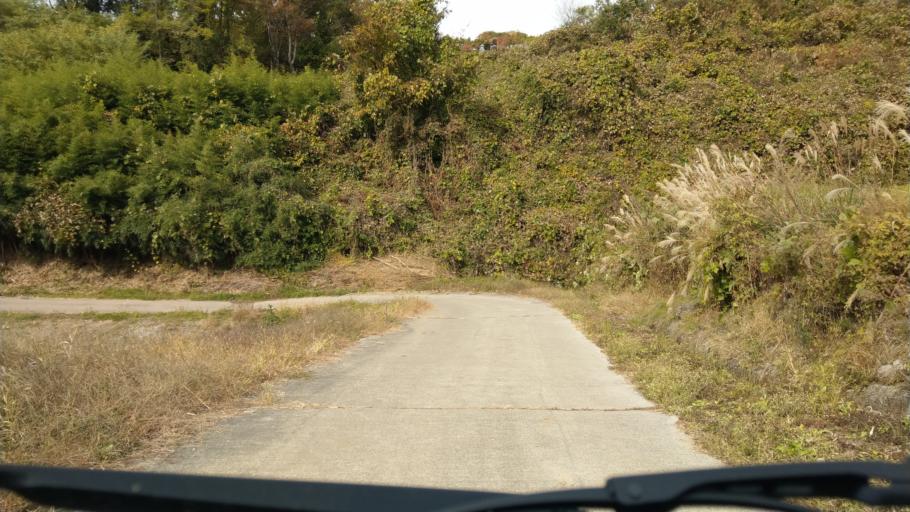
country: JP
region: Nagano
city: Komoro
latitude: 36.3516
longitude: 138.4351
